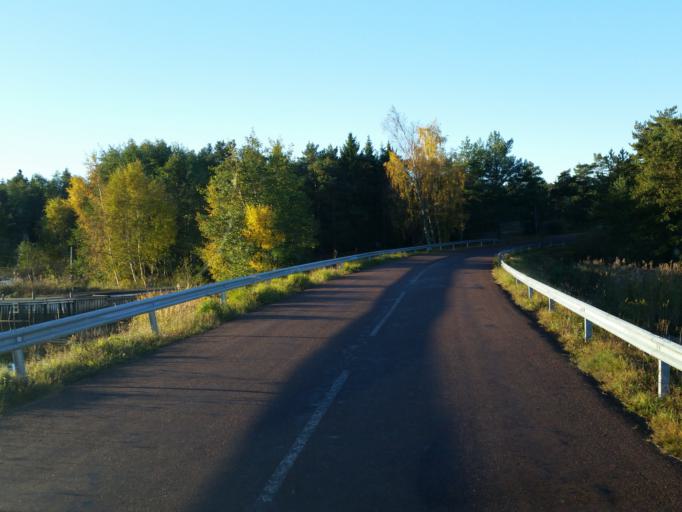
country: AX
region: Alands skaergard
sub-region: Vardoe
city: Vardoe
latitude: 60.2716
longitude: 20.3903
